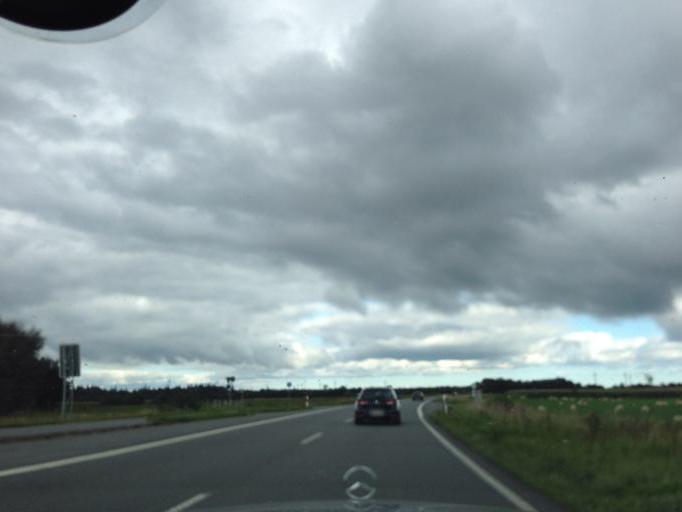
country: DE
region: Schleswig-Holstein
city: Horup
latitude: 54.7481
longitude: 9.0789
